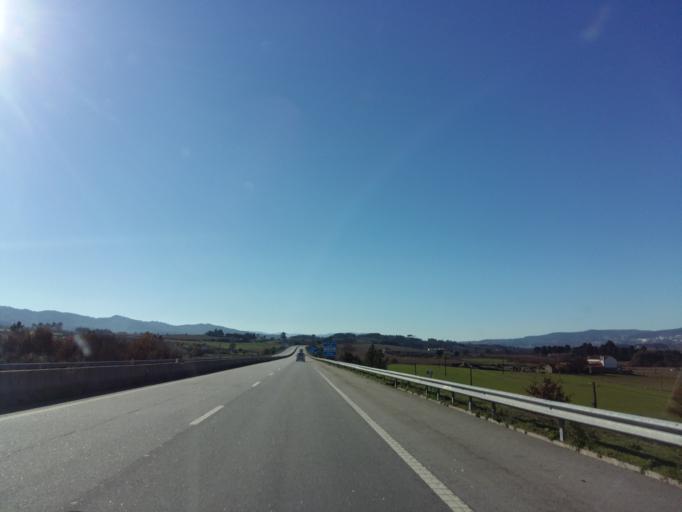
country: PT
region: Castelo Branco
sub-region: Covilha
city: Teixoso
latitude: 40.2594
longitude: -7.4430
